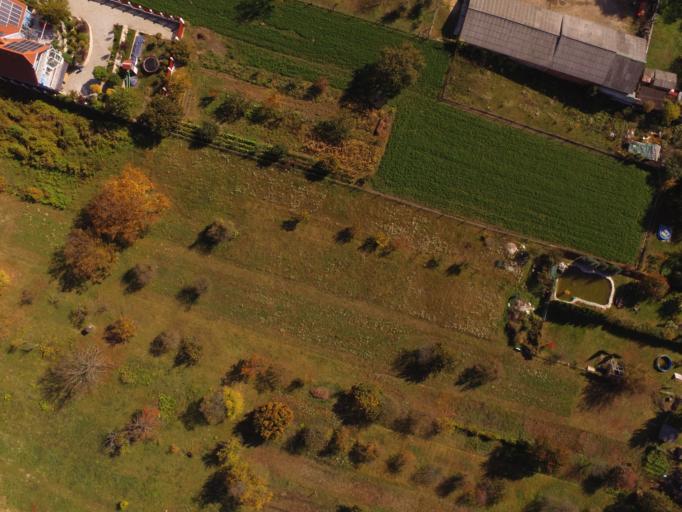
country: HU
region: Fejer
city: Many
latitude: 47.5200
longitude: 18.6175
